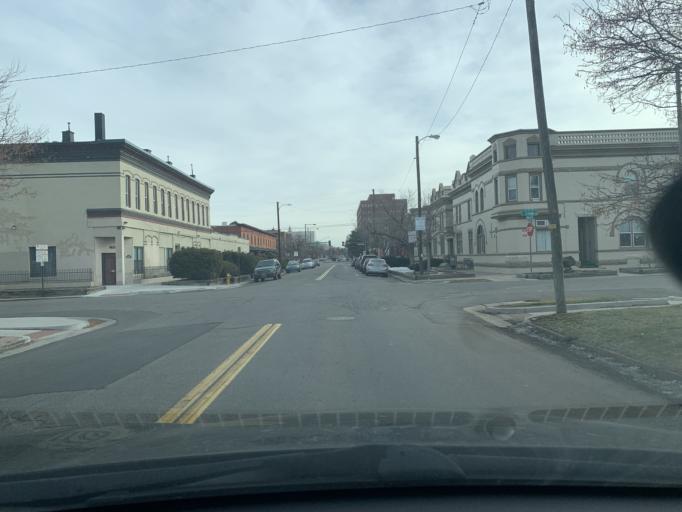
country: US
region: Colorado
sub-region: Denver County
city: Denver
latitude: 39.7384
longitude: -105.0019
